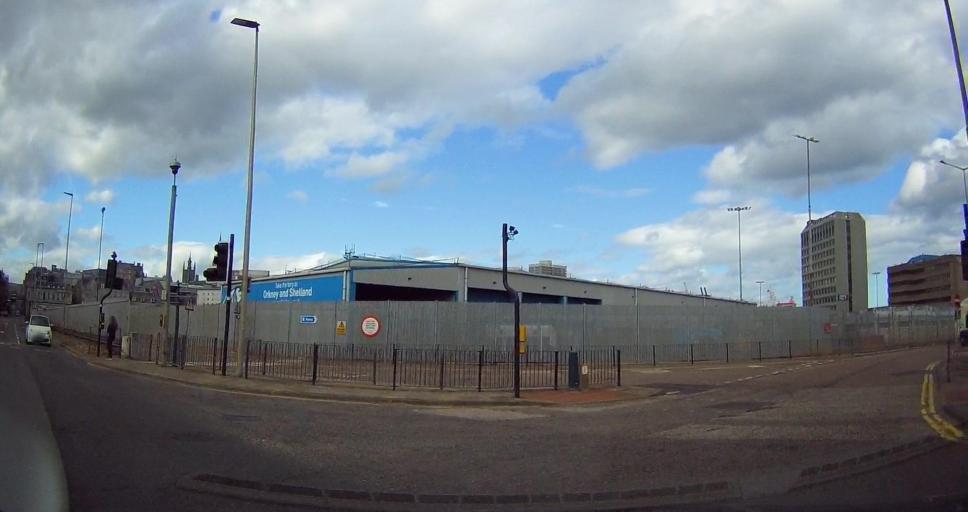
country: GB
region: Scotland
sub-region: Aberdeen City
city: Aberdeen
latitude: 57.1430
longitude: -2.0929
